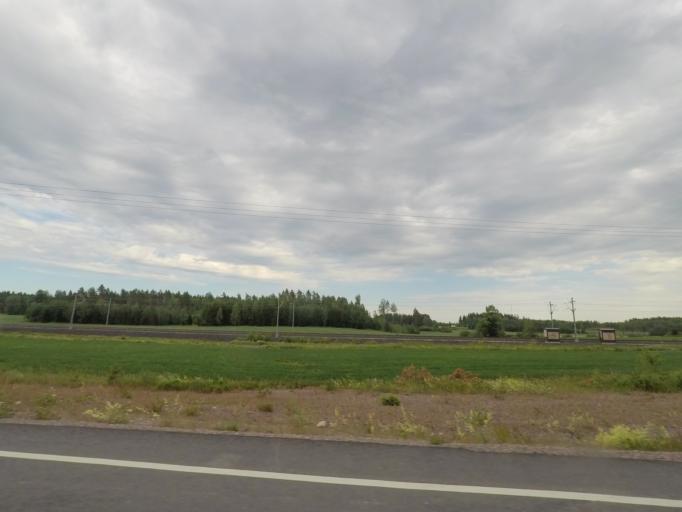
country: FI
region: Uusimaa
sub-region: Helsinki
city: Maentsaelae
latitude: 60.6827
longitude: 25.3650
